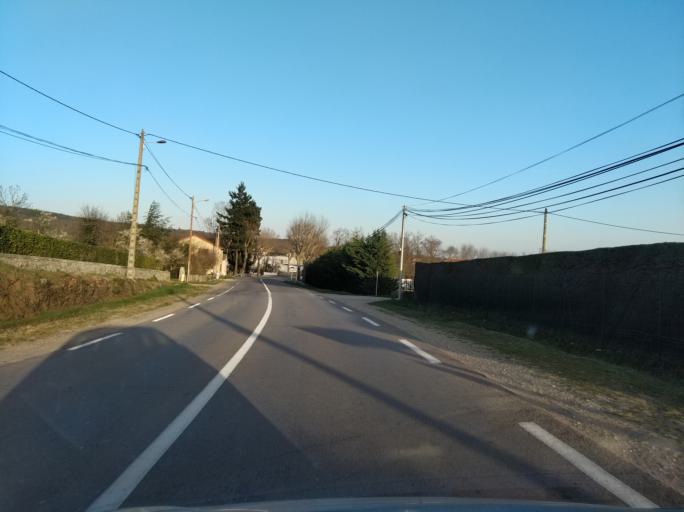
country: FR
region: Rhone-Alpes
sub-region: Departement de l'Ardeche
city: Boulieu-les-Annonay
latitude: 45.2696
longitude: 4.6774
